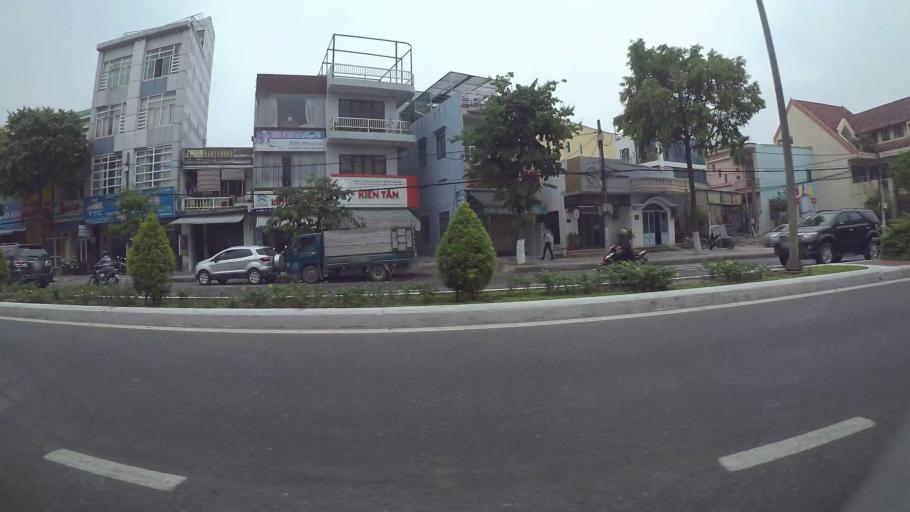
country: VN
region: Da Nang
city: Cam Le
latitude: 16.0296
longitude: 108.2233
